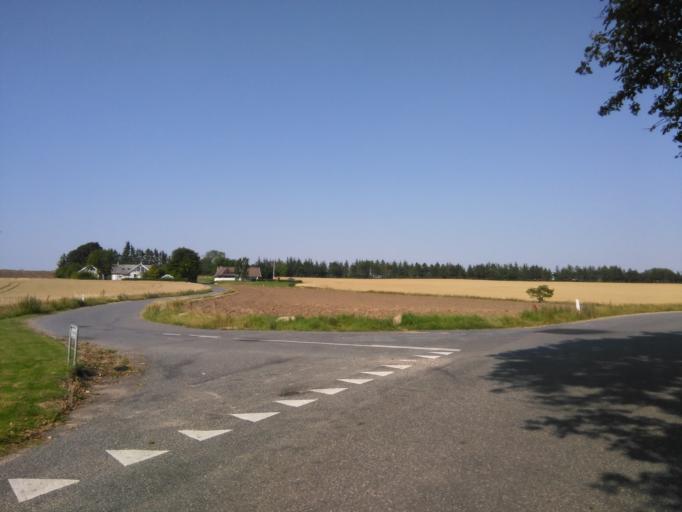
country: DK
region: Central Jutland
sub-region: Arhus Kommune
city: Framlev
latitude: 56.1384
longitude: 10.0221
